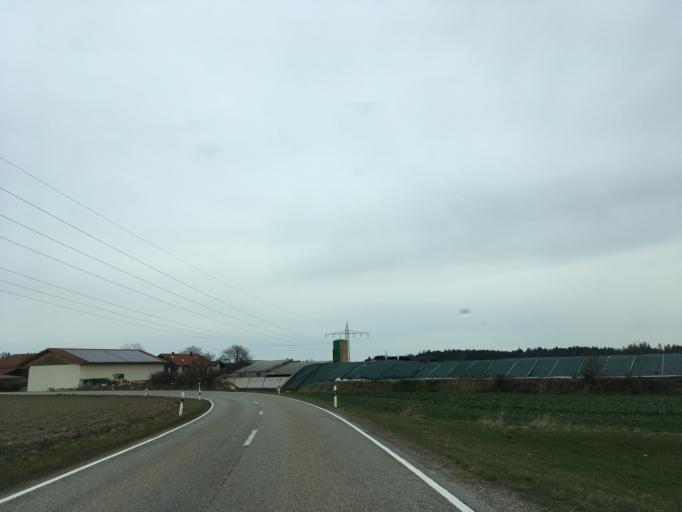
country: DE
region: Bavaria
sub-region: Upper Bavaria
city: Schnaitsee
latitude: 48.0722
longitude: 12.3917
